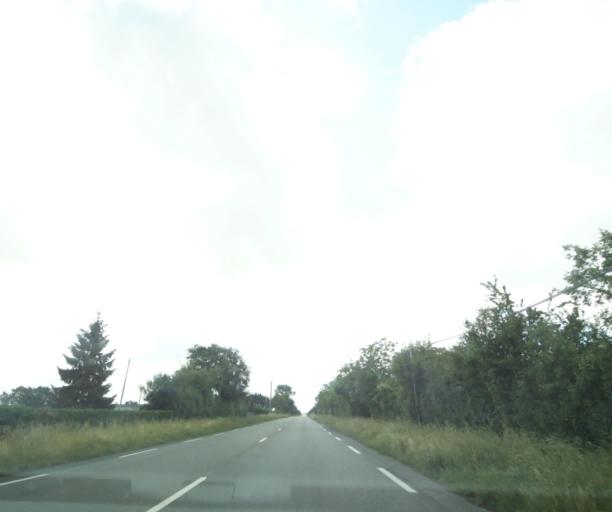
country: FR
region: Pays de la Loire
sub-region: Departement de la Sarthe
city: Vion
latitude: 47.7881
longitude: -0.2425
